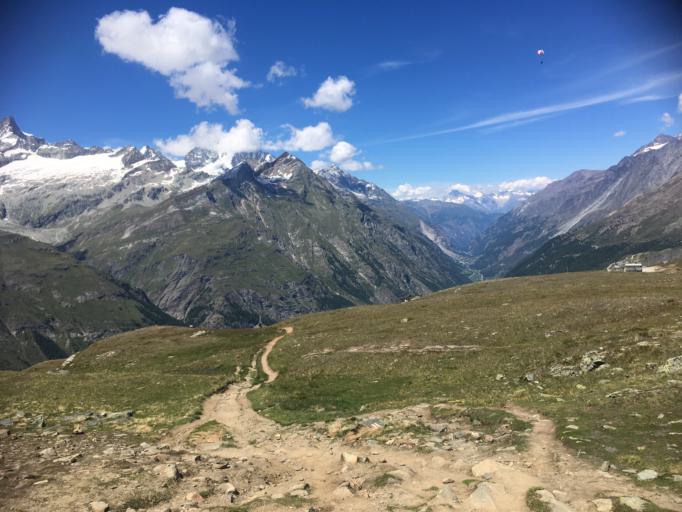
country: CH
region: Valais
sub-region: Visp District
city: Zermatt
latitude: 45.9890
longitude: 7.7524
